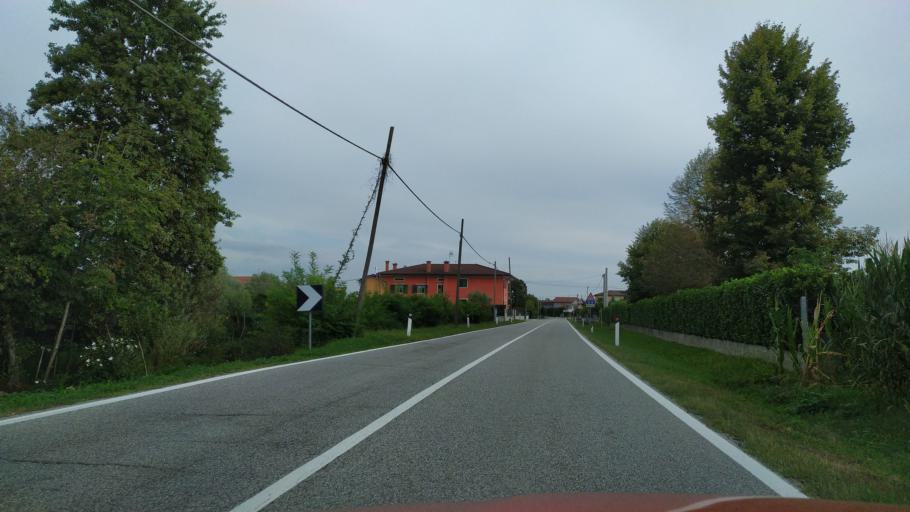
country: IT
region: Veneto
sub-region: Provincia di Padova
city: San Giorgio in Bosco
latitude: 45.5829
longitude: 11.7796
